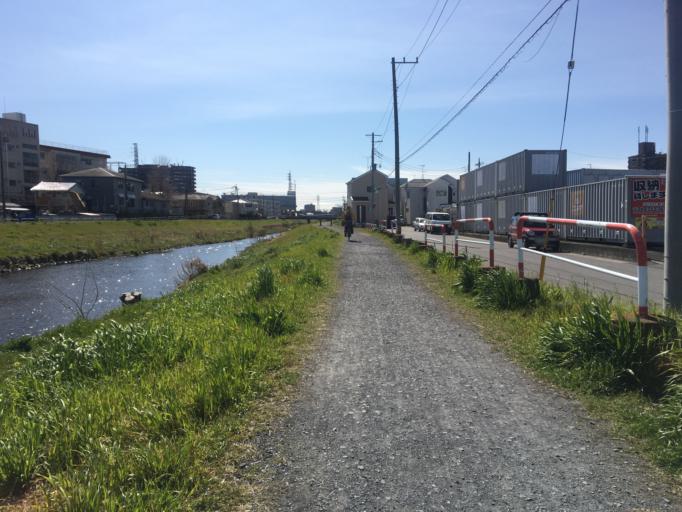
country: JP
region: Saitama
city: Asaka
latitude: 35.8025
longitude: 139.5822
